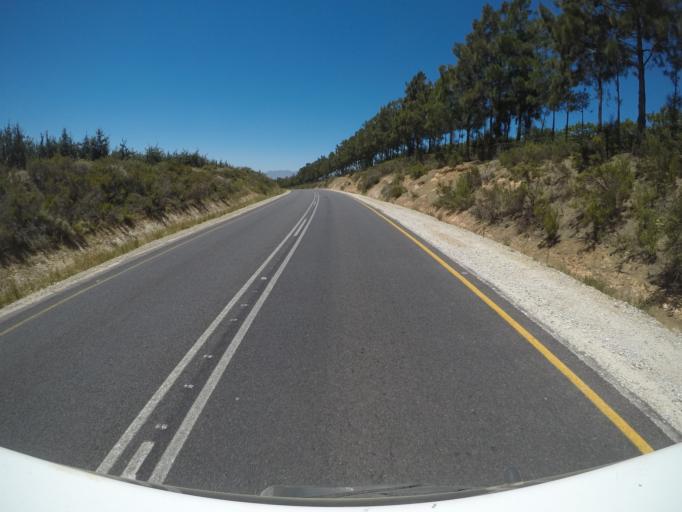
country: ZA
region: Western Cape
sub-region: Overberg District Municipality
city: Grabouw
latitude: -34.0675
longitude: 19.1294
